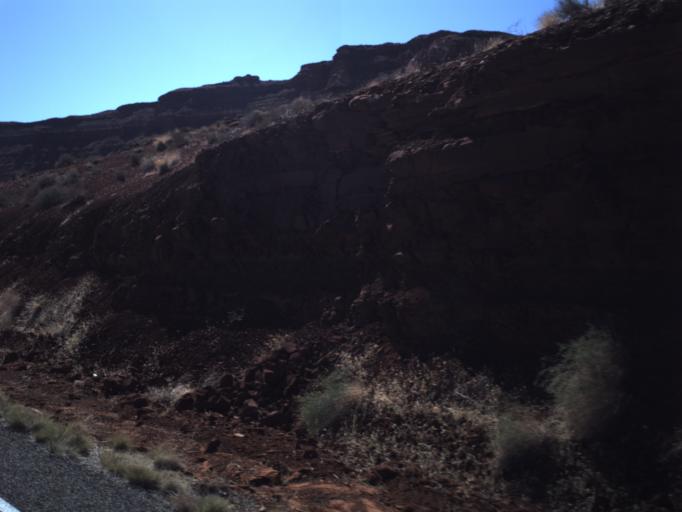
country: US
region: Utah
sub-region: San Juan County
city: Blanding
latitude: 37.8784
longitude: -110.3521
